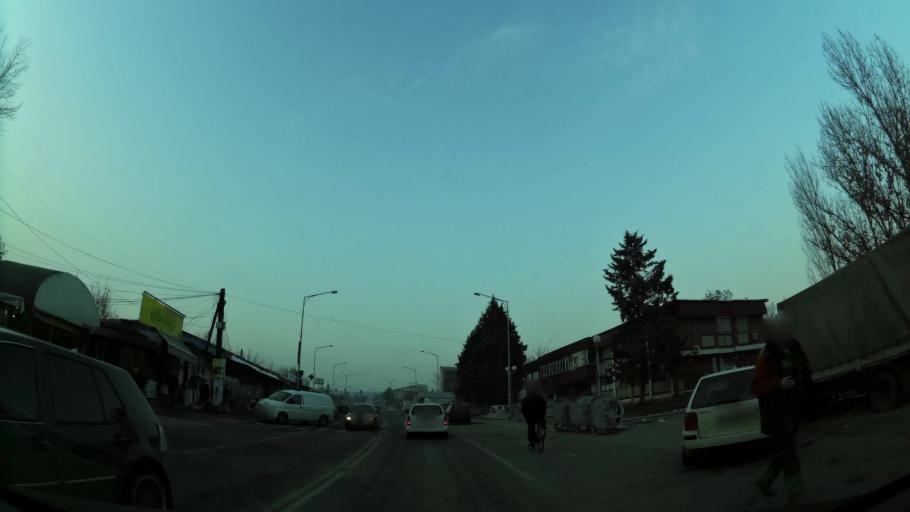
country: MK
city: Creshevo
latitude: 42.0050
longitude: 21.5040
